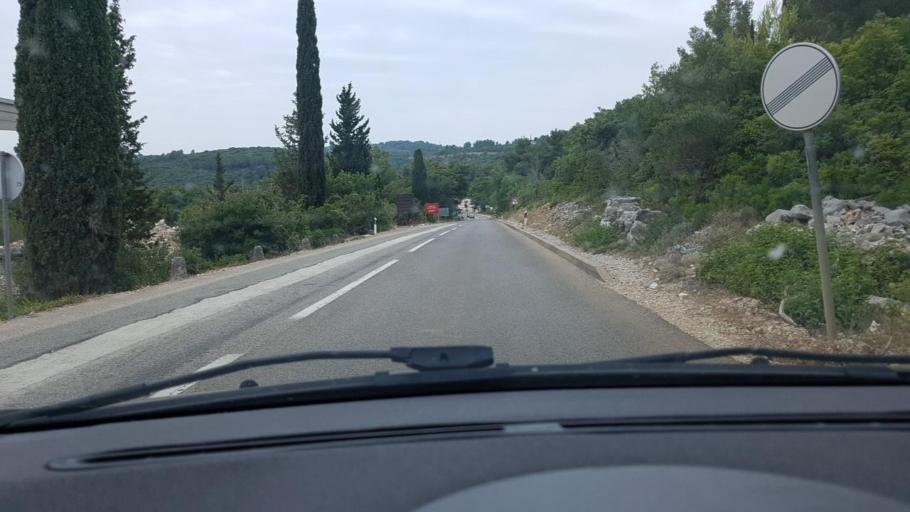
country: HR
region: Dubrovacko-Neretvanska
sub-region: Grad Korcula
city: Zrnovo
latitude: 42.9532
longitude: 17.1262
